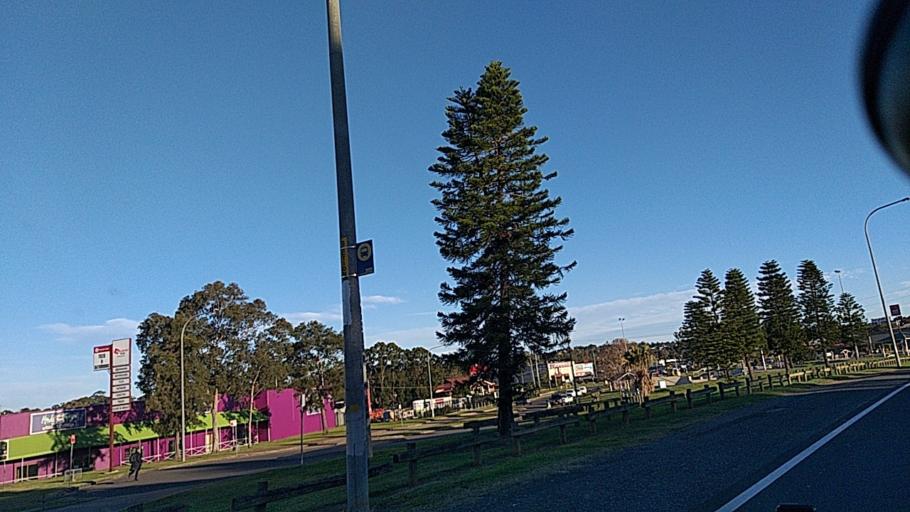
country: AU
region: New South Wales
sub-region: Campbelltown Municipality
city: Leumeah
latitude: -34.0480
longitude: 150.8284
